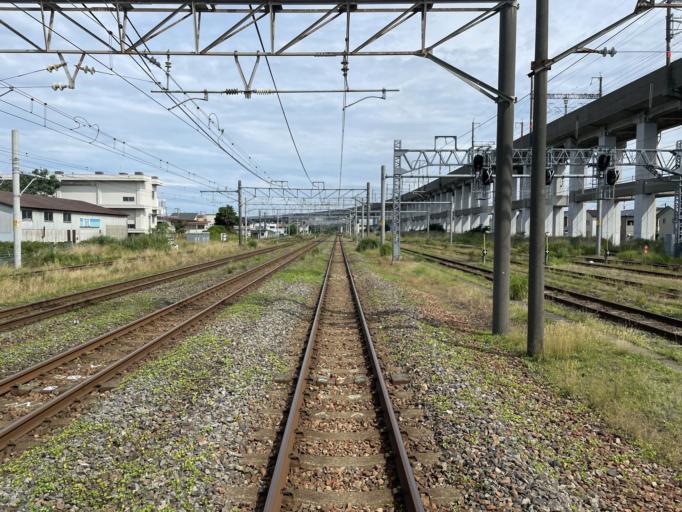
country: JP
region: Niigata
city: Kameda-honcho
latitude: 37.9101
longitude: 139.0803
